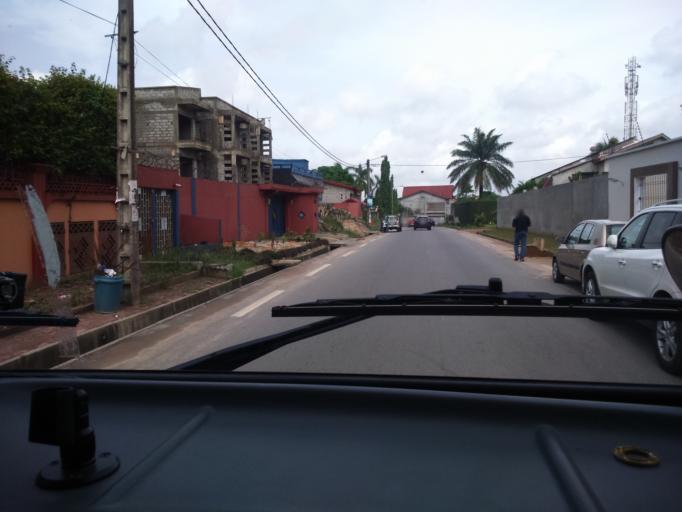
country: CI
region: Lagunes
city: Abidjan
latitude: 5.3567
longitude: -3.9798
